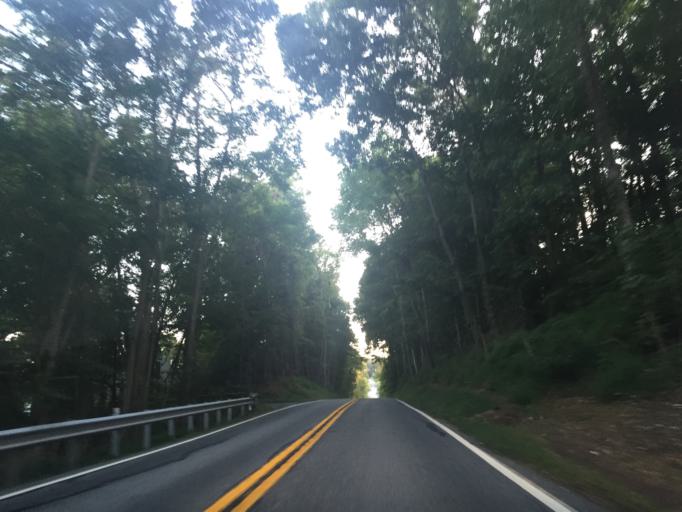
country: US
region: Pennsylvania
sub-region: York County
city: Susquehanna Trails
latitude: 39.6637
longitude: -76.3266
